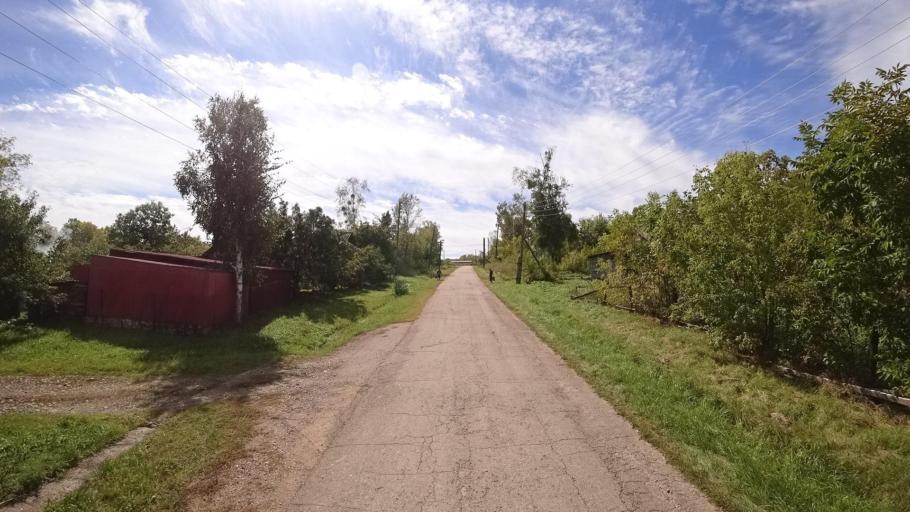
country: RU
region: Primorskiy
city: Yakovlevka
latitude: 44.6569
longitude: 133.7453
